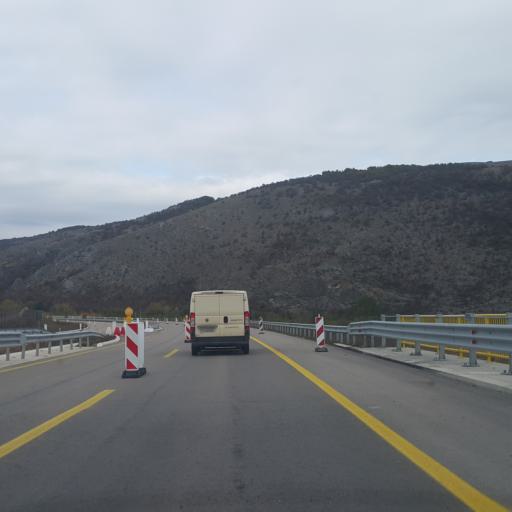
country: RS
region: Central Serbia
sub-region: Pirotski Okrug
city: Bela Palanka
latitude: 43.2310
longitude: 22.3799
